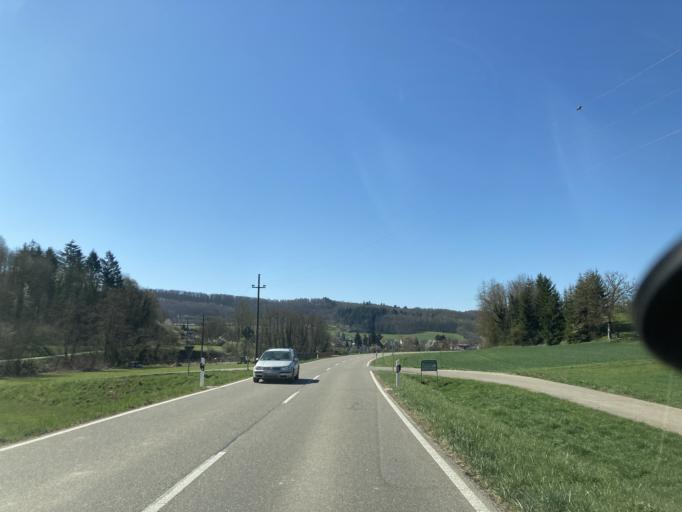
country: DE
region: Baden-Wuerttemberg
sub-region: Freiburg Region
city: Schliengen
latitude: 47.7461
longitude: 7.6098
